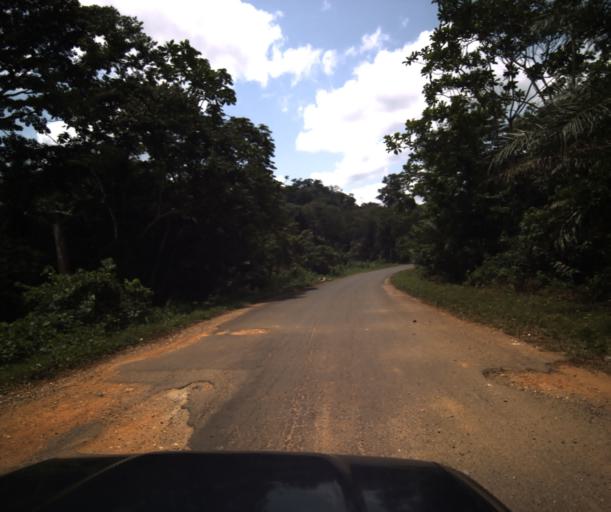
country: CM
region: Centre
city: Eseka
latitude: 3.8286
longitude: 10.8095
